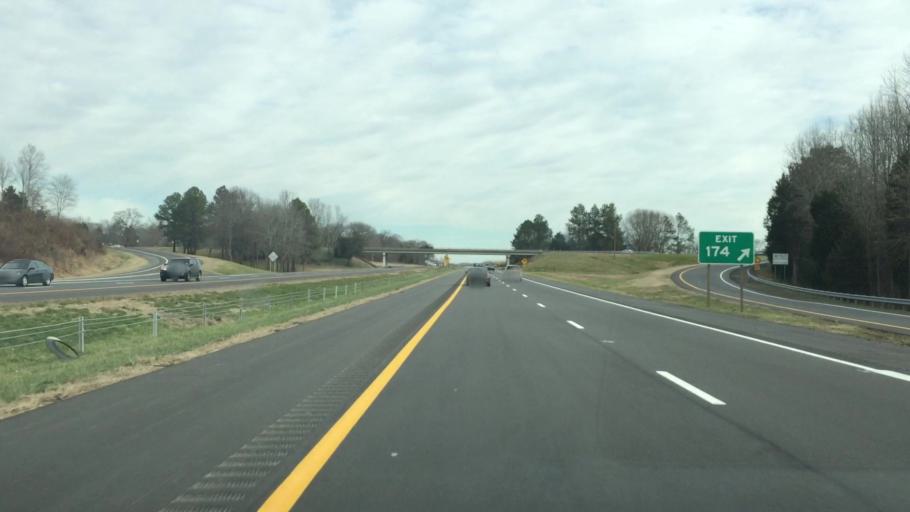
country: US
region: North Carolina
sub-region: Davie County
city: Mocksville
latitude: 35.9550
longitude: -80.5348
